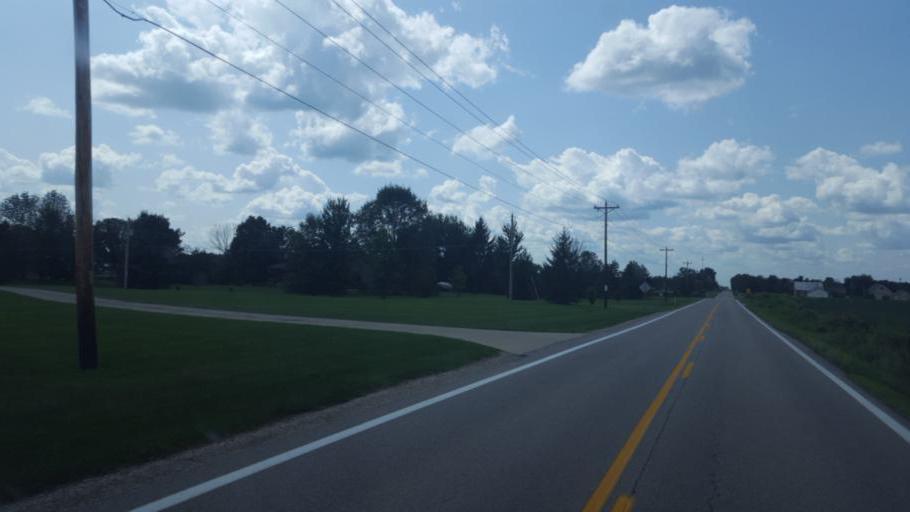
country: US
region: Ohio
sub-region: Delaware County
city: Sunbury
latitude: 40.3246
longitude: -82.8764
